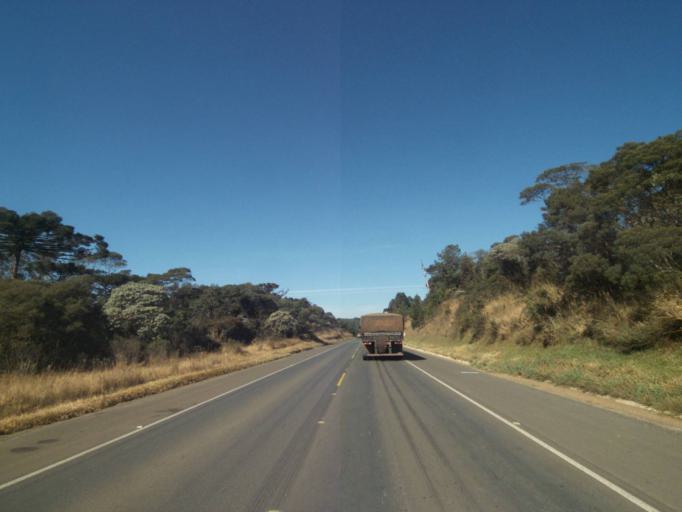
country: BR
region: Parana
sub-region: Tibagi
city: Tibagi
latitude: -24.5705
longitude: -50.4521
